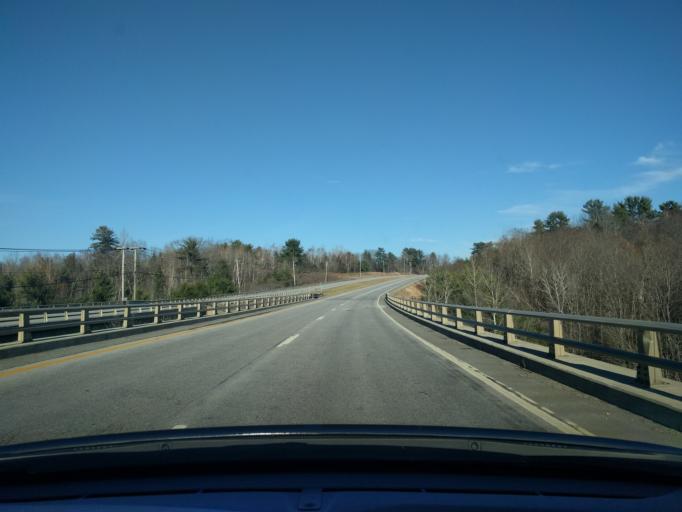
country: US
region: Maine
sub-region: Penobscot County
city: Hampden
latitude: 44.7495
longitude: -68.8451
